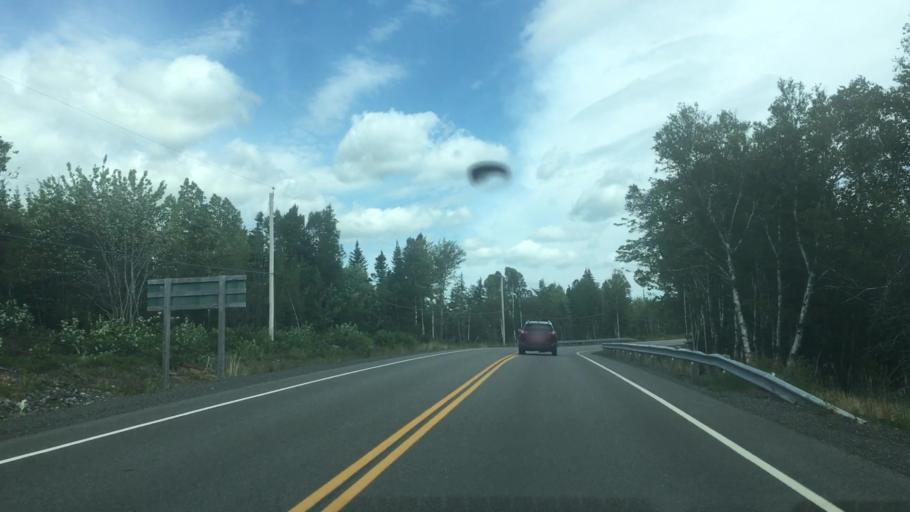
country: CA
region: Nova Scotia
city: Sydney Mines
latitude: 46.3094
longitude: -60.6167
